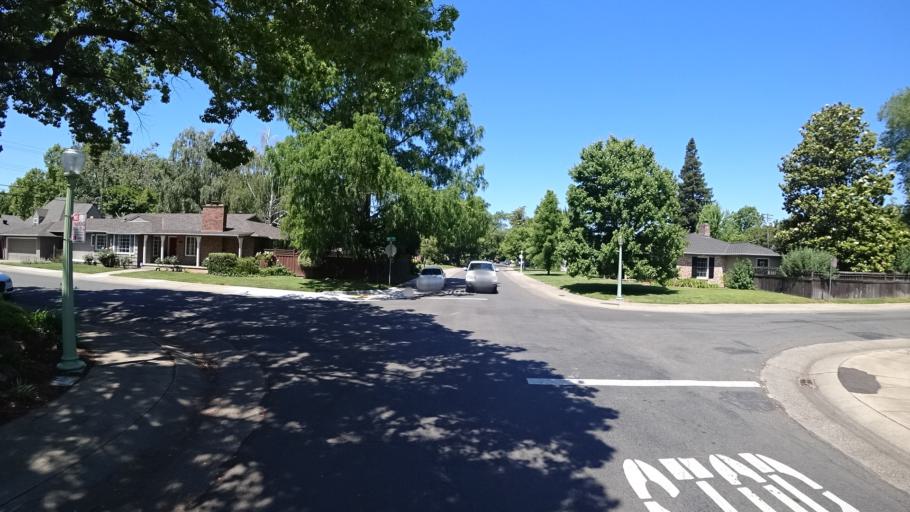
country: US
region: California
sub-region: Sacramento County
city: Sacramento
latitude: 38.5467
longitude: -121.4933
